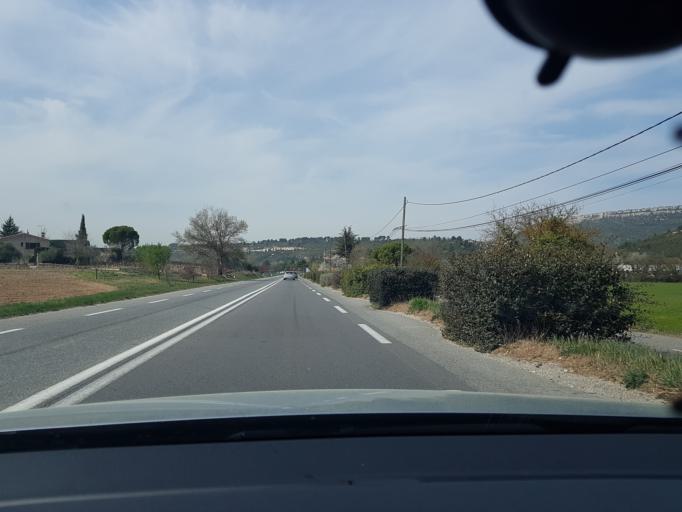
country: FR
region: Provence-Alpes-Cote d'Azur
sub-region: Departement des Bouches-du-Rhone
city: Chateauneuf-le-Rouge
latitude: 43.4747
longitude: 5.5753
